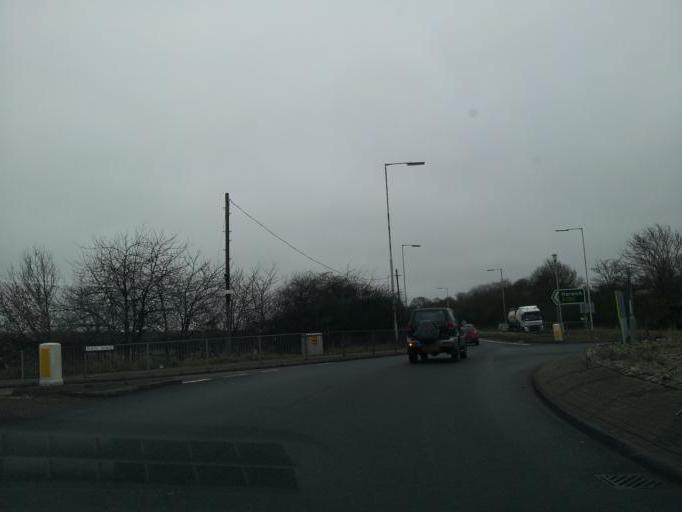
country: GB
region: England
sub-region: Suffolk
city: Shotley Gate
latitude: 51.9277
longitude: 1.2182
